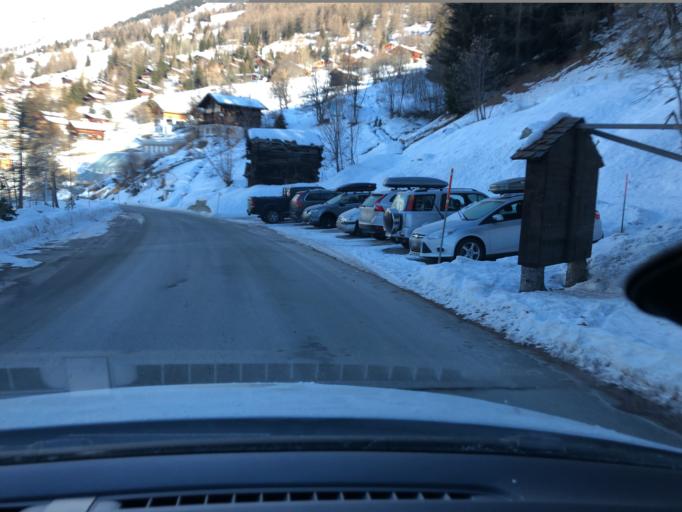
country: CH
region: Valais
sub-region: Goms District
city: Fiesch
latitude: 46.4269
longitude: 8.1584
